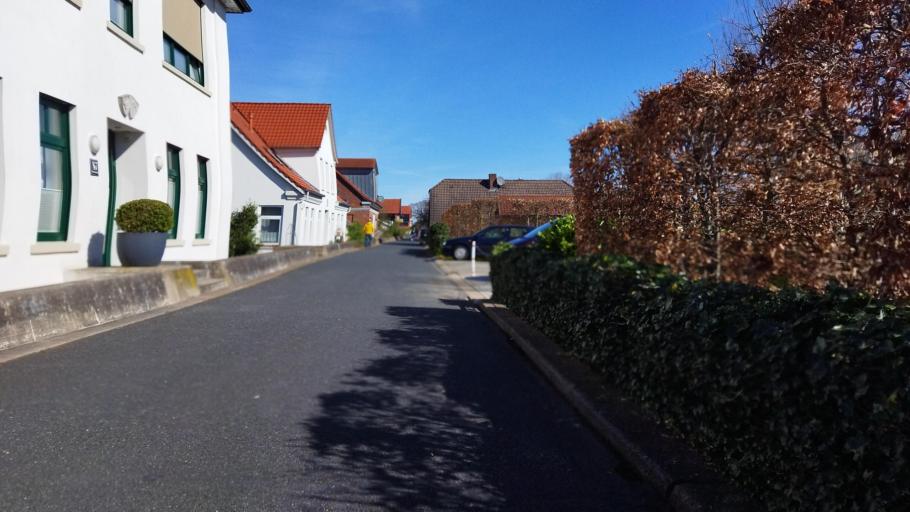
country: DE
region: Lower Saxony
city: Elsfleth
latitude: 53.2398
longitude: 8.4652
